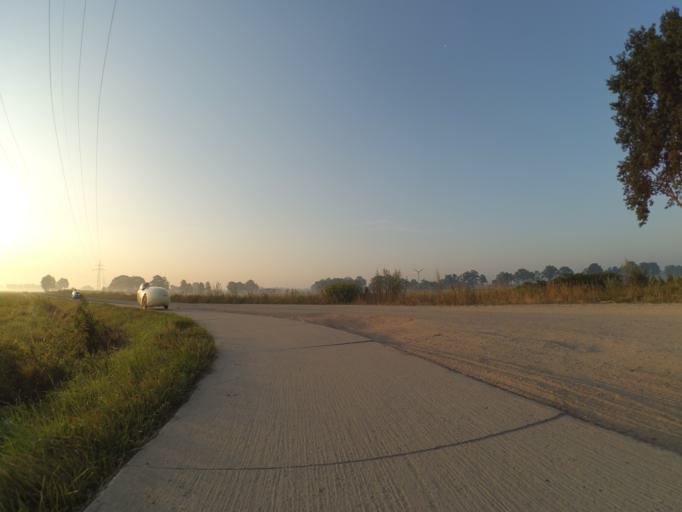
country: NL
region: Overijssel
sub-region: Gemeente Almelo
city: Almelo
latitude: 52.3935
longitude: 6.6954
